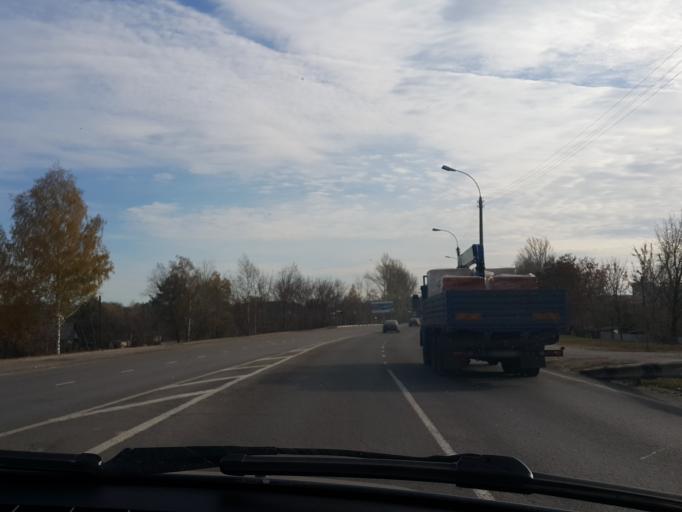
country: RU
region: Tambov
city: Tambov
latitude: 52.7186
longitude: 41.5014
